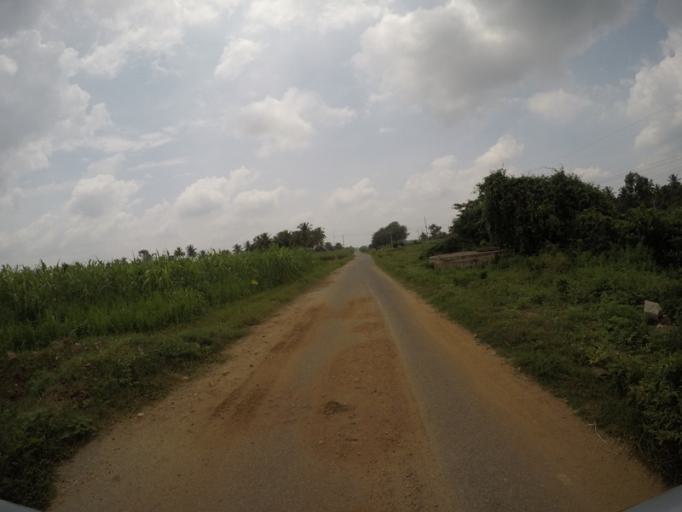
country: IN
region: Karnataka
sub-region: Ramanagara
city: Kanakapura
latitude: 12.7408
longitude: 77.4862
